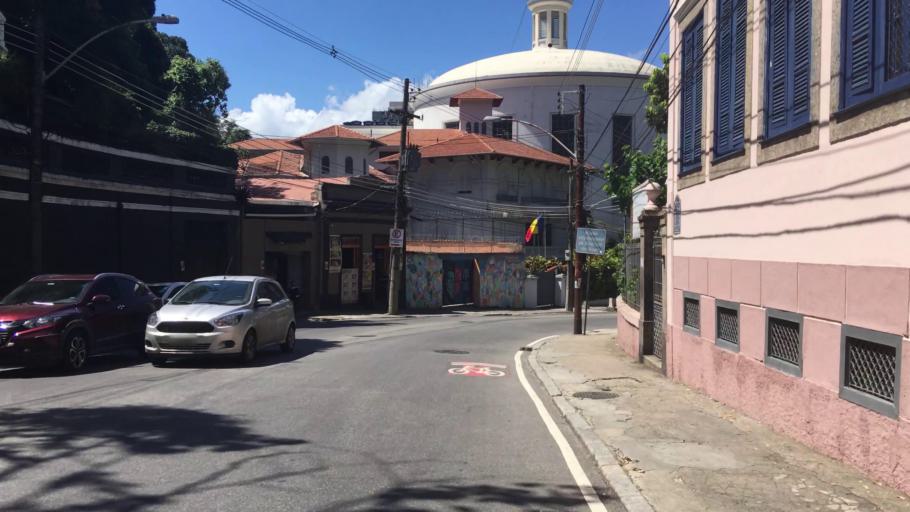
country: BR
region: Rio de Janeiro
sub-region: Rio De Janeiro
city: Rio de Janeiro
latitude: -22.9402
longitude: -43.1994
